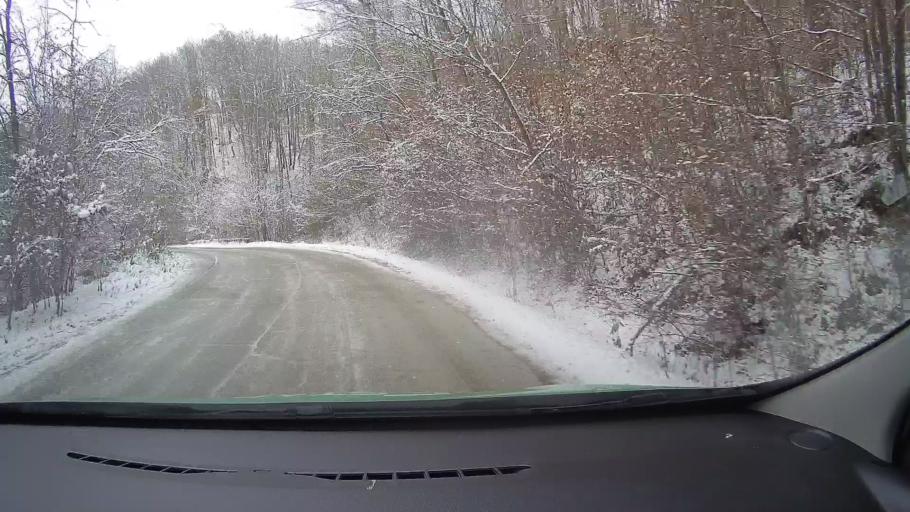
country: RO
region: Alba
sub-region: Oras Zlatna
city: Zlatna
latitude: 46.0964
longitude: 23.1799
